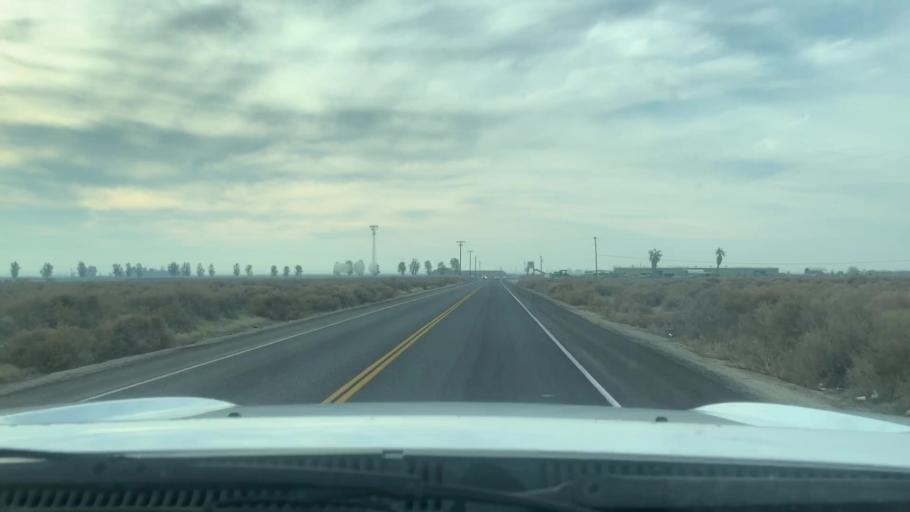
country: US
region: California
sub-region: Kern County
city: Buttonwillow
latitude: 35.4998
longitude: -119.5411
